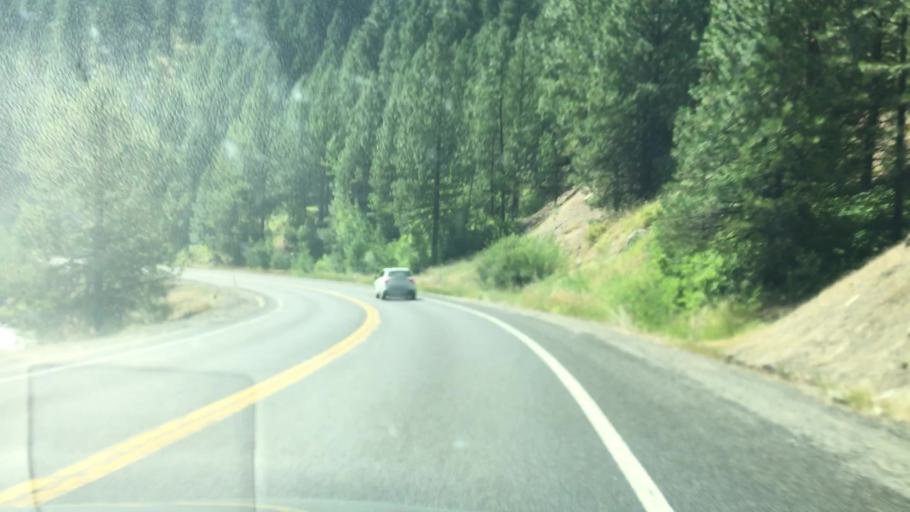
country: US
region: Idaho
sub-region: Valley County
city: Cascade
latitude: 44.2509
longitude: -116.0903
